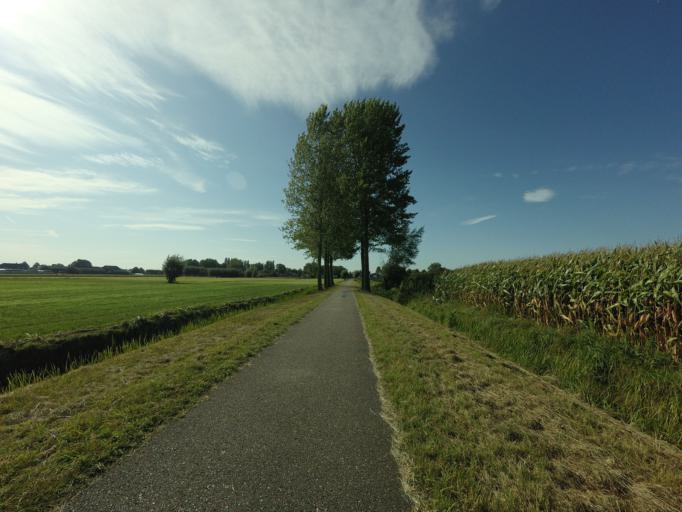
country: NL
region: South Holland
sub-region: Gemeente Leerdam
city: Leerdam
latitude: 51.9215
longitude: 5.0707
